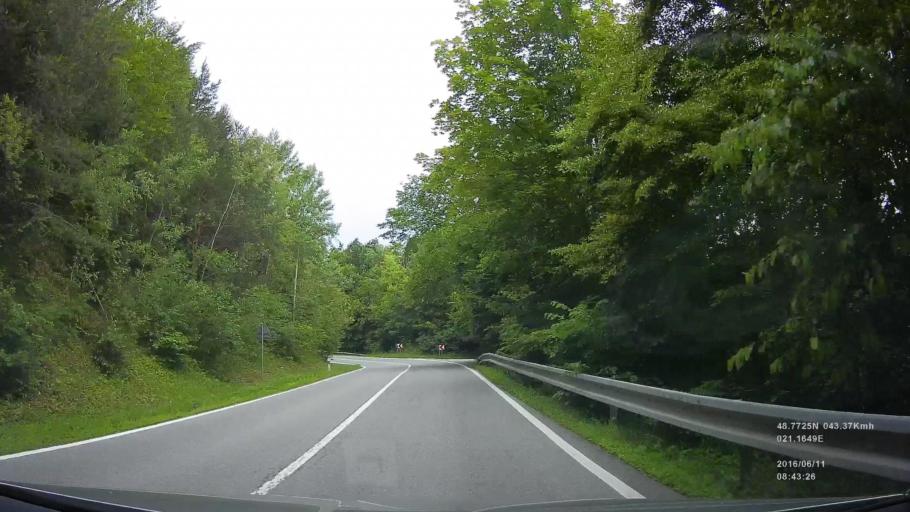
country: SK
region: Kosicky
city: Kosice
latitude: 48.7675
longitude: 21.1658
